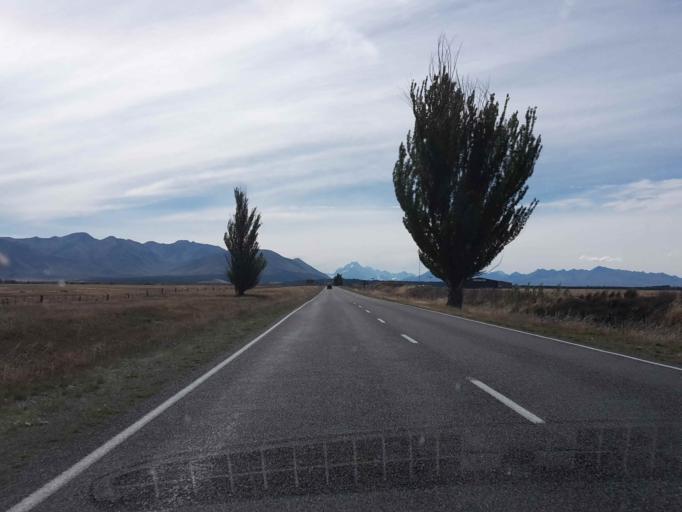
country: NZ
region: Canterbury
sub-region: Timaru District
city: Pleasant Point
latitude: -44.2472
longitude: 170.1164
